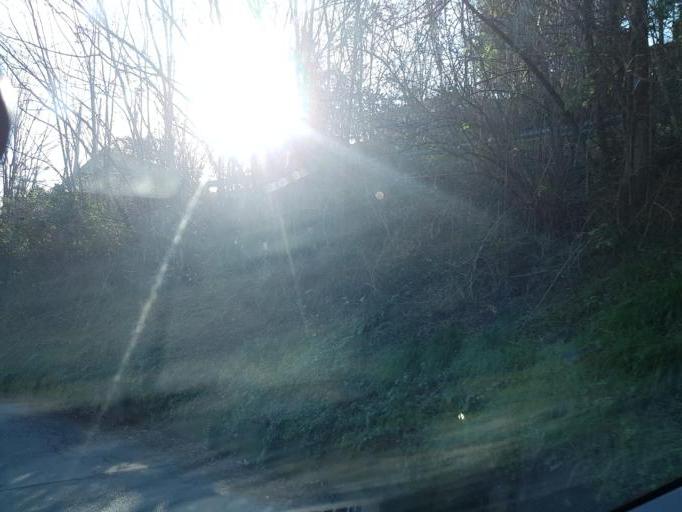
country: IT
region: Liguria
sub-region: Provincia di Genova
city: Campomorone
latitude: 44.5092
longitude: 8.8756
